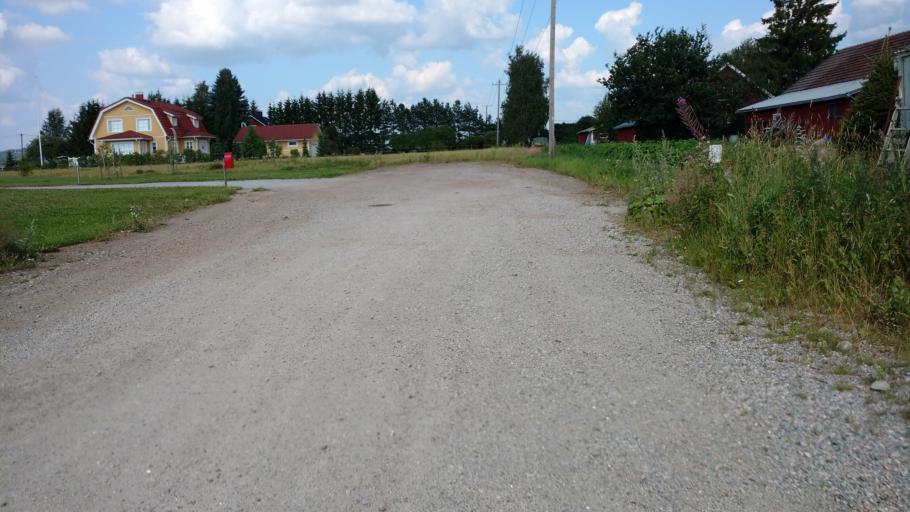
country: FI
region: Varsinais-Suomi
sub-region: Salo
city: Salo
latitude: 60.4048
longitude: 23.1678
